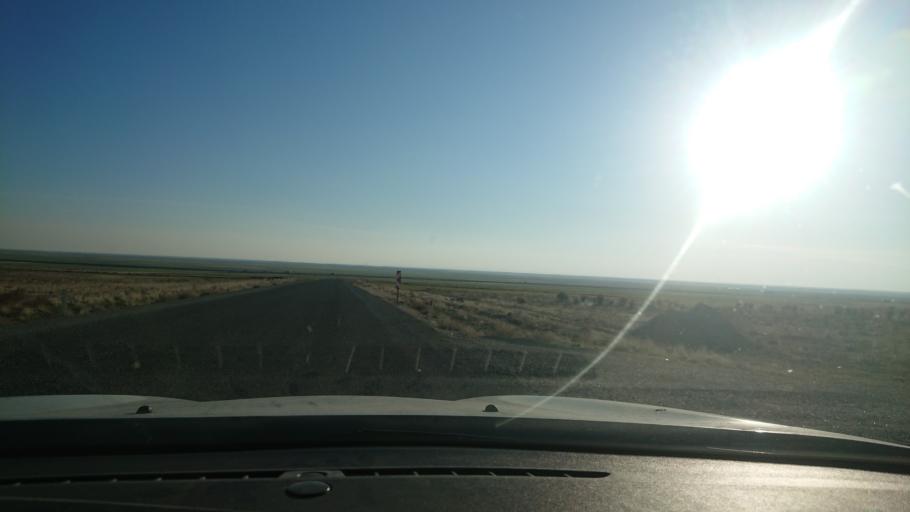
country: TR
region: Aksaray
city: Acipinar
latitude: 38.6720
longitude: 33.7270
